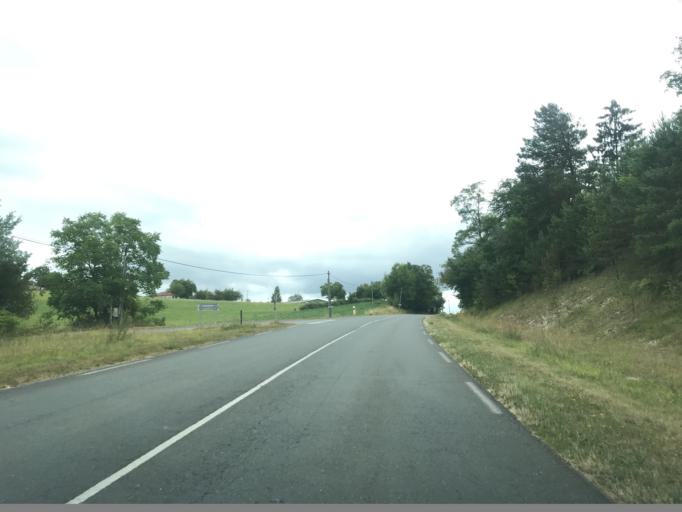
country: FR
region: Aquitaine
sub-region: Departement de la Dordogne
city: Brantome
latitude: 45.4097
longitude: 0.5725
